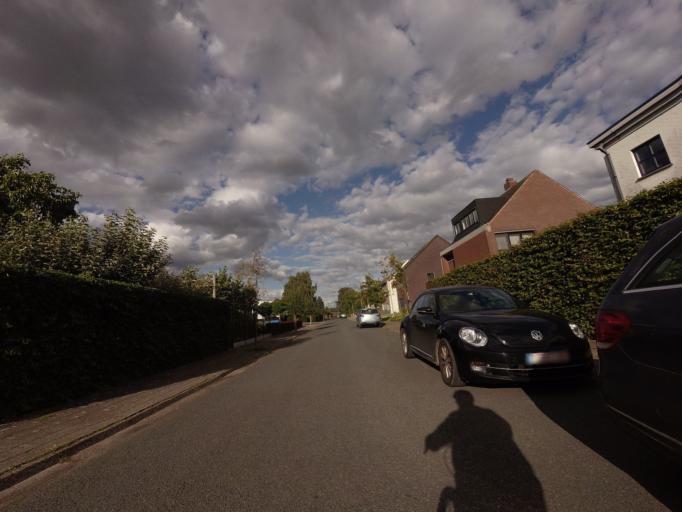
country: BE
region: Flanders
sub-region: Provincie Vlaams-Brabant
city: Kapelle-op-den-Bos
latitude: 51.0001
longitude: 4.3577
